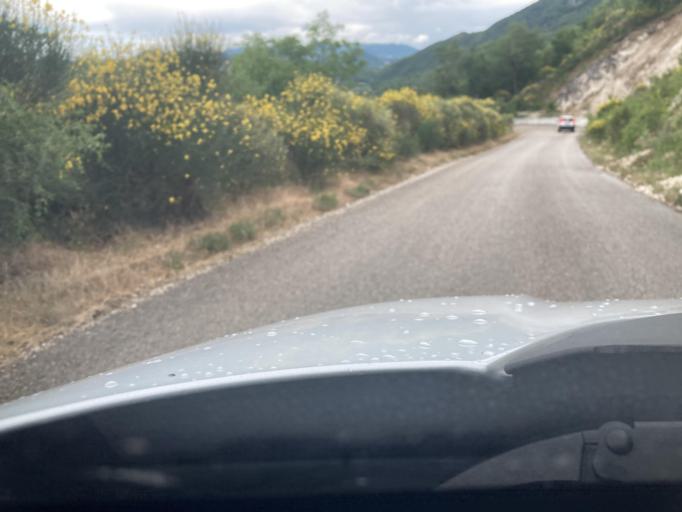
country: IT
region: Abruzzo
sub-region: Provincia dell' Aquila
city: Fossa
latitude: 42.2893
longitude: 13.4909
